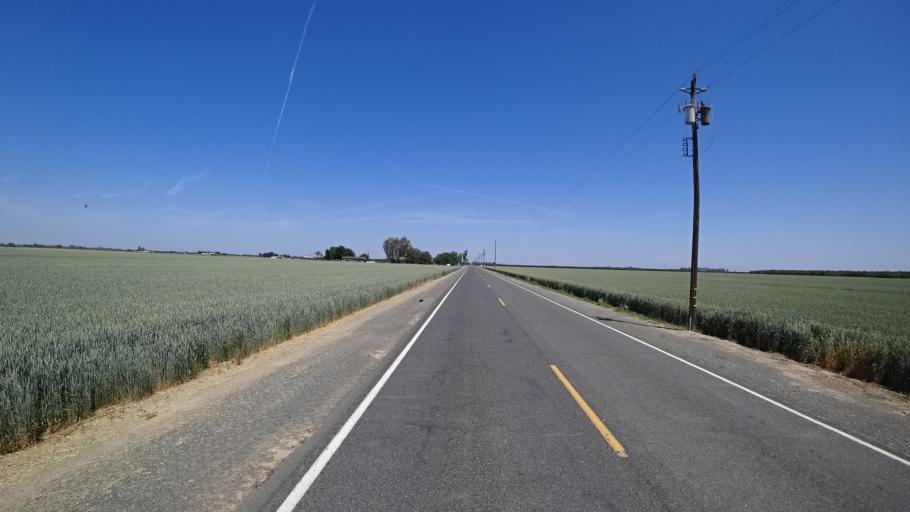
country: US
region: California
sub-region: Kings County
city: Armona
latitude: 36.2283
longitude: -119.7088
